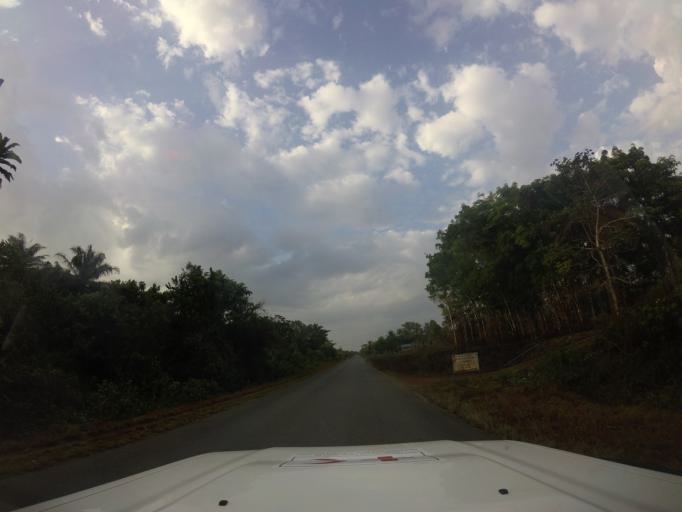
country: LR
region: Bomi
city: Tubmanburg
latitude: 6.7752
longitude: -10.8456
